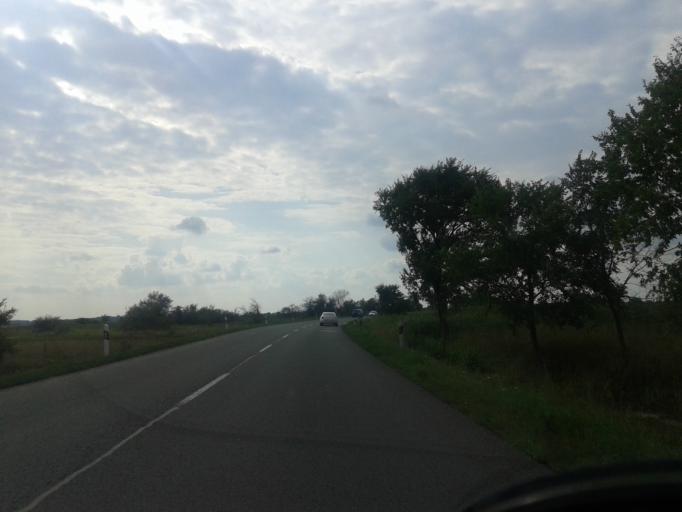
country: HU
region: Bacs-Kiskun
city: Akaszto
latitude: 46.7423
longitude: 19.1459
